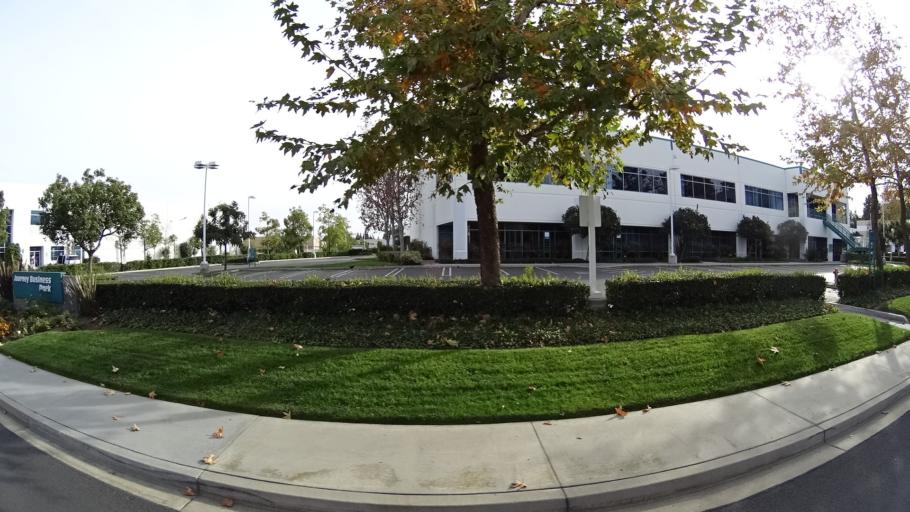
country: US
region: California
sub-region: Orange County
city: Aliso Viejo
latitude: 33.5695
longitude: -117.7282
